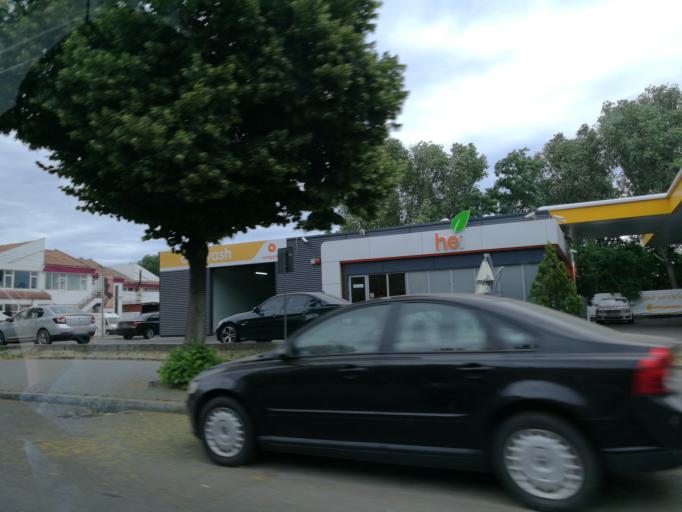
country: RO
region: Constanta
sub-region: Municipiul Constanta
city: Palazu Mare
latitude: 44.2150
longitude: 28.6284
